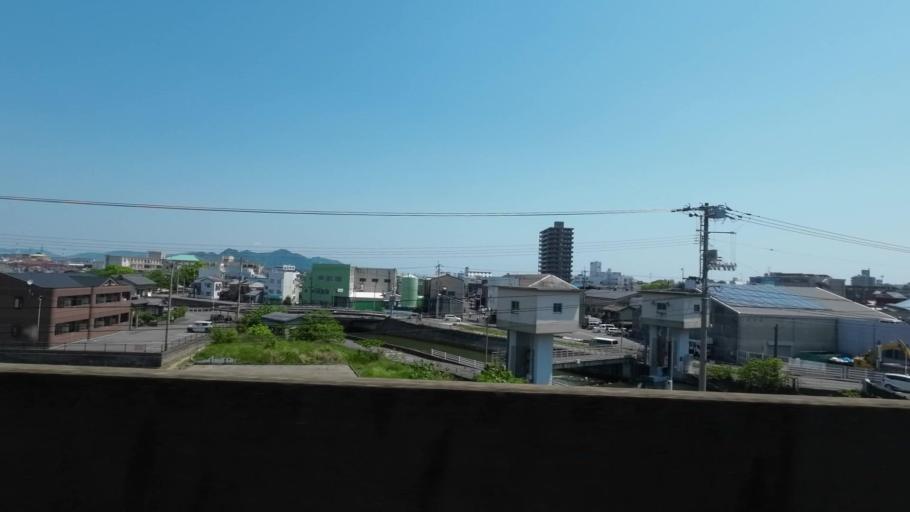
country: JP
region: Ehime
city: Hojo
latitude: 34.0680
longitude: 132.9902
